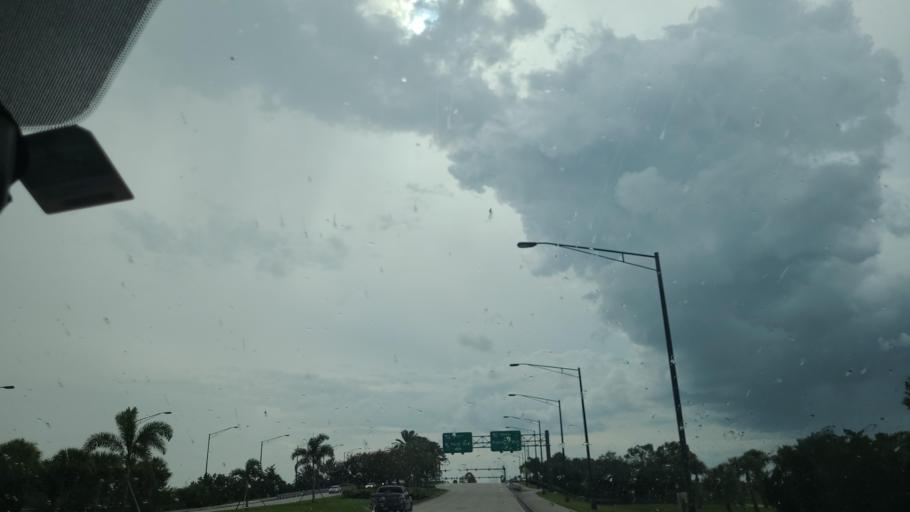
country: US
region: Florida
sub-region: Saint Lucie County
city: Port Saint Lucie
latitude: 27.2098
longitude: -80.3960
